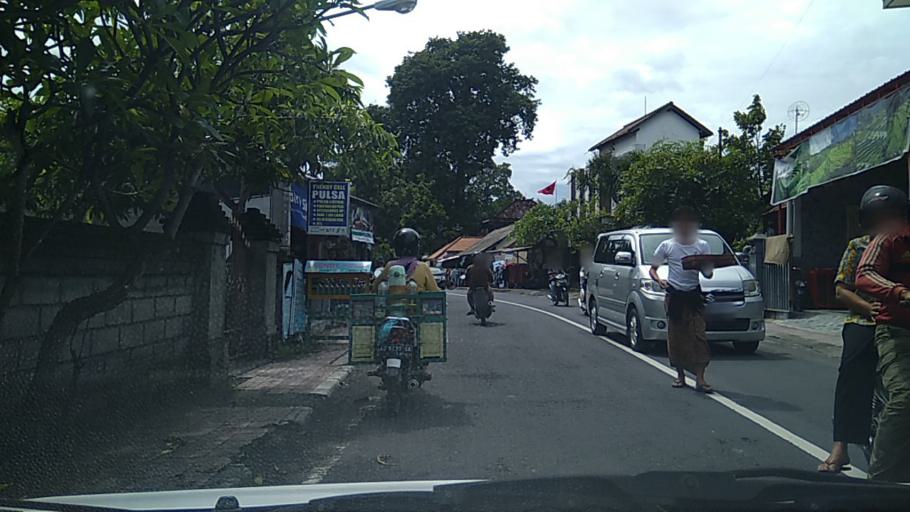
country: ID
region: Bali
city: Dajan Tangluk
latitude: -8.6472
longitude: 115.2457
